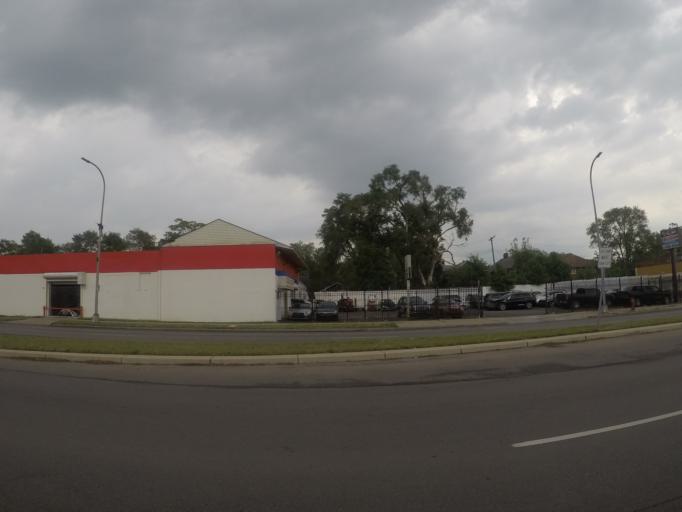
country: US
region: Michigan
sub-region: Wayne County
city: Highland Park
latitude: 42.3703
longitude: -83.1390
